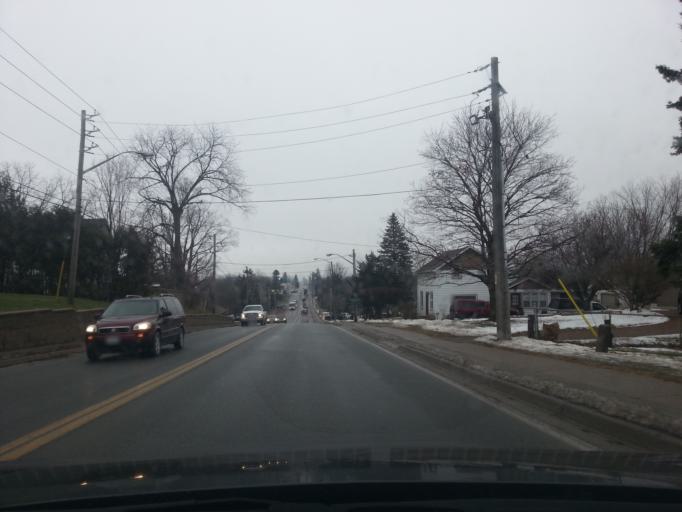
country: CA
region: Ontario
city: Uxbridge
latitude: 44.0987
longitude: -78.9508
